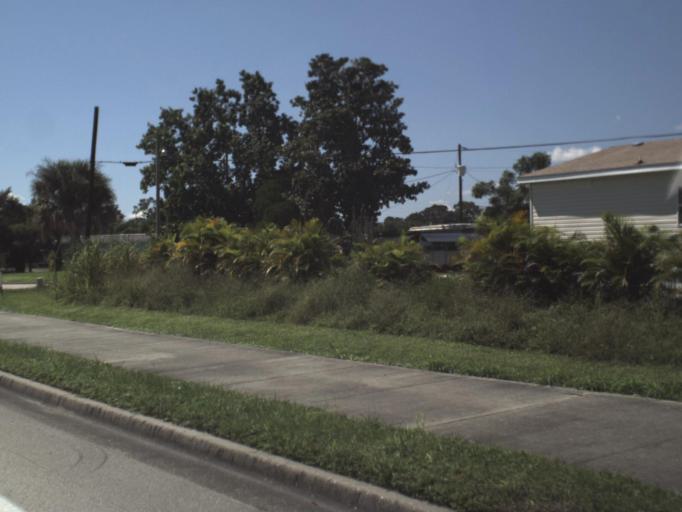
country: US
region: Florida
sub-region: Lee County
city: Suncoast Estates
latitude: 26.6938
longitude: -81.8561
